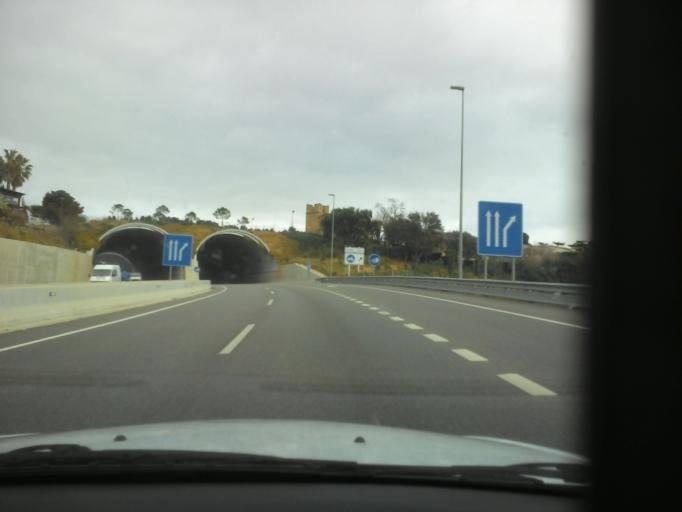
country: ES
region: Catalonia
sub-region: Provincia de Girona
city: Castell-Platja d'Aro
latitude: 41.8225
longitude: 3.0574
